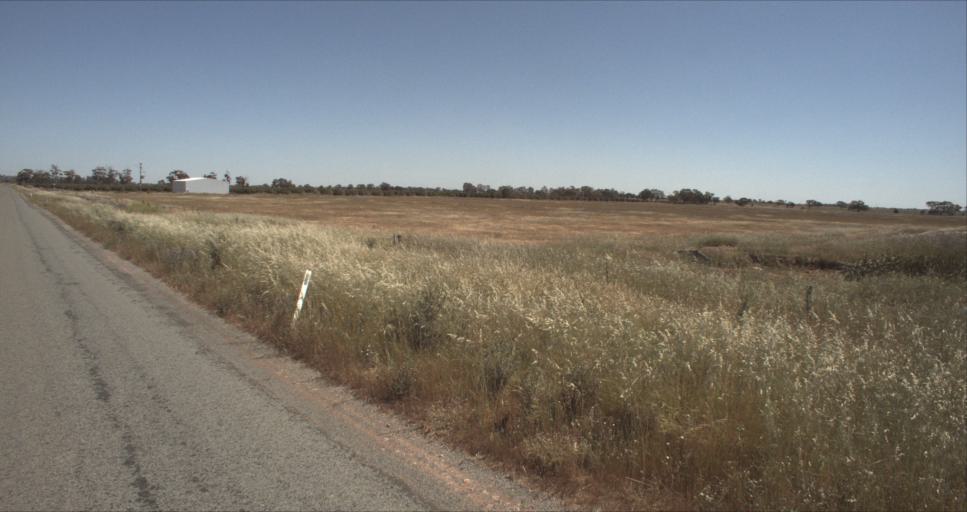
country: AU
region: New South Wales
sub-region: Leeton
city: Leeton
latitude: -34.4854
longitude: 146.4143
